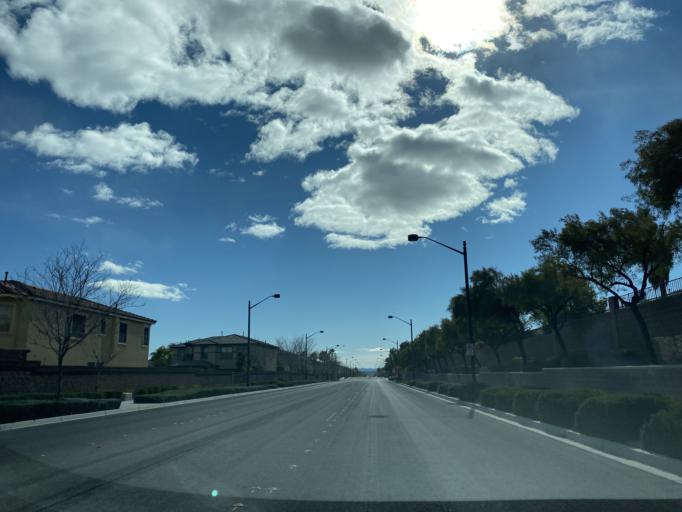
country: US
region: Nevada
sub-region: Clark County
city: Summerlin South
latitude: 36.2937
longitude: -115.3014
